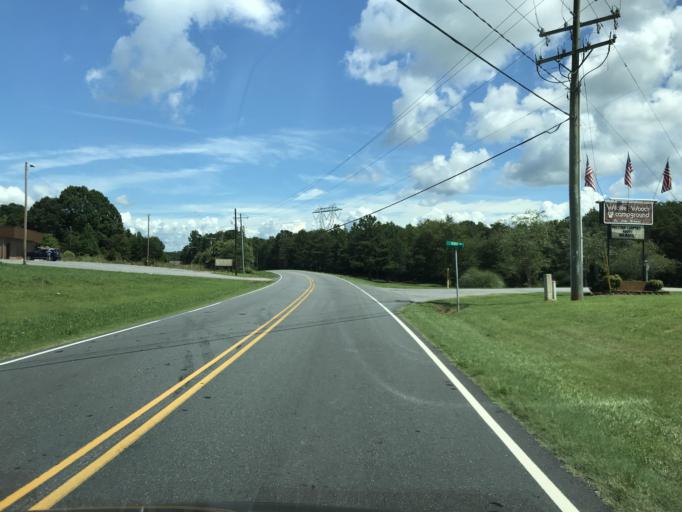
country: US
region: North Carolina
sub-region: Catawba County
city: Lake Norman of Catawba
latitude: 35.5706
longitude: -81.0329
